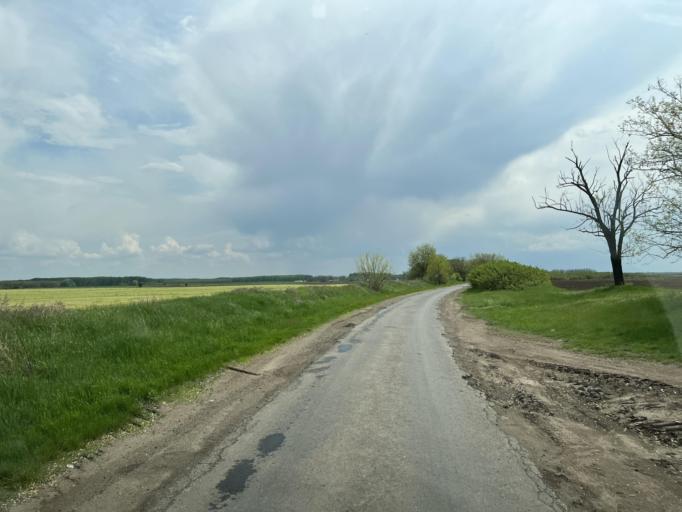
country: HU
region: Pest
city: Nagykoros
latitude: 46.9918
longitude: 19.8035
